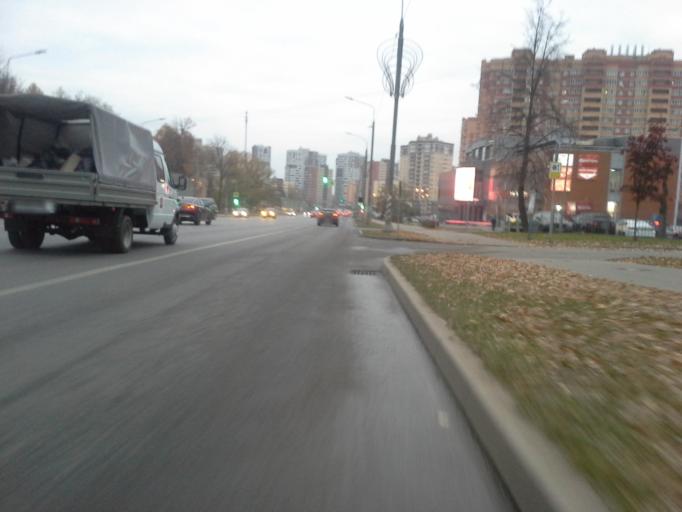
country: RU
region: Moskovskaya
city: Kommunarka
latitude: 55.5738
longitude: 37.4733
